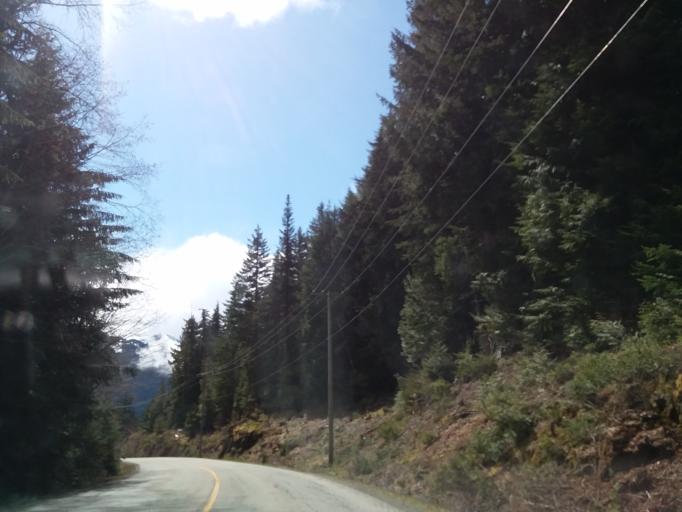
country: CA
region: British Columbia
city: Whistler
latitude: 50.1347
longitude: -122.9821
